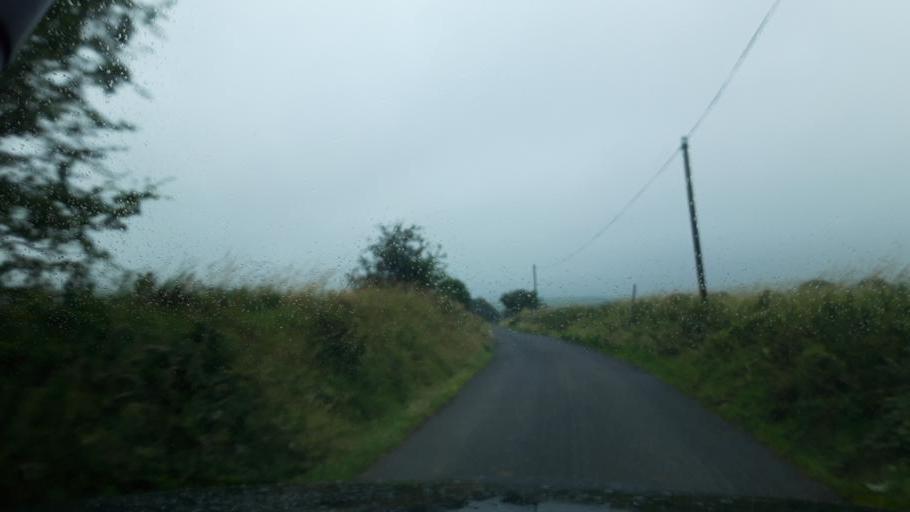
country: IE
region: Leinster
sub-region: Kilkenny
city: Callan
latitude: 52.6353
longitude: -7.5370
